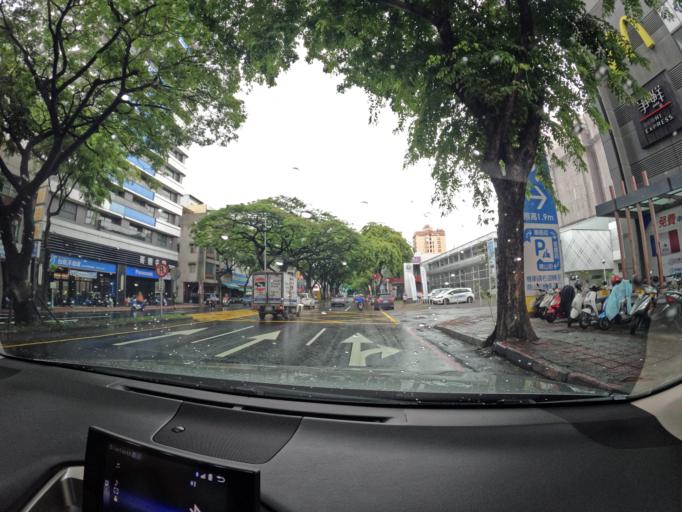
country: TW
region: Kaohsiung
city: Kaohsiung
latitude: 22.6530
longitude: 120.3195
